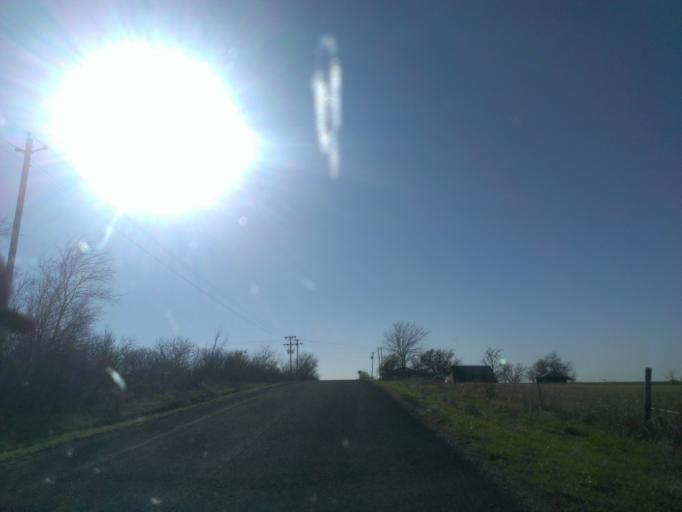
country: US
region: Texas
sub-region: Bastrop County
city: Elgin
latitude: 30.4722
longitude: -97.2732
